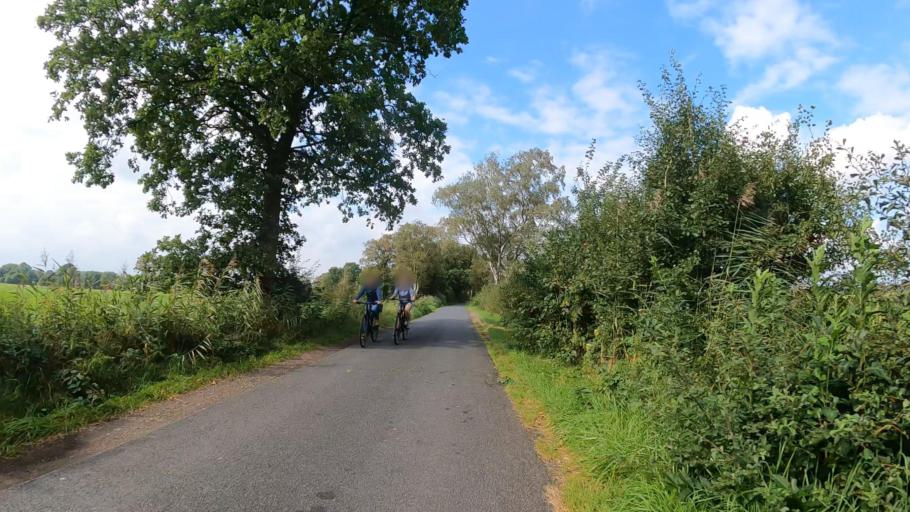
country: DE
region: Schleswig-Holstein
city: Tornesch
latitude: 53.7227
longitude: 9.6974
